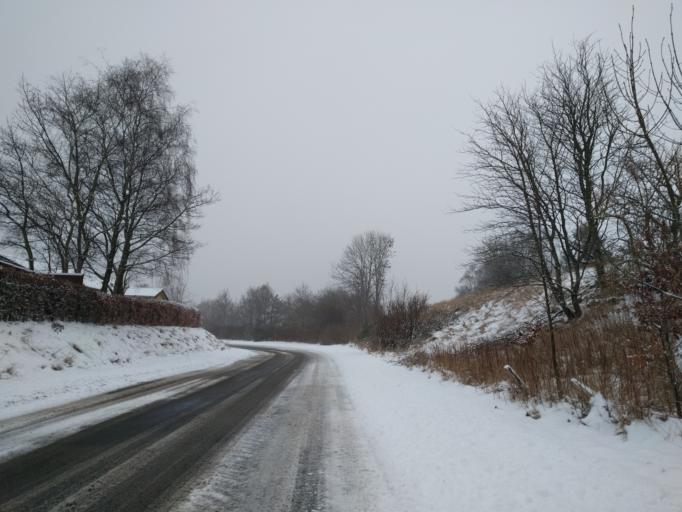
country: DK
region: Central Jutland
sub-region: Viborg Kommune
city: Viborg
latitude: 56.4318
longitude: 9.3997
